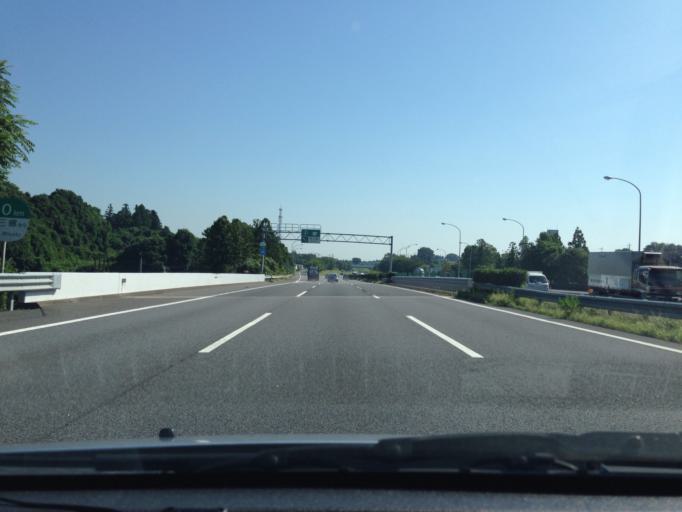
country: JP
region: Ibaraki
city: Ishioka
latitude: 36.1434
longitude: 140.2085
